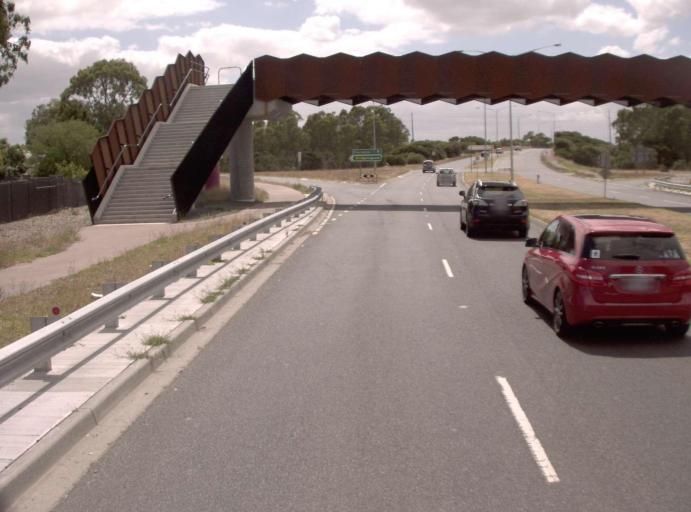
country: AU
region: Victoria
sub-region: Kingston
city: Patterson Lakes
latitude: -38.0677
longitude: 145.1456
